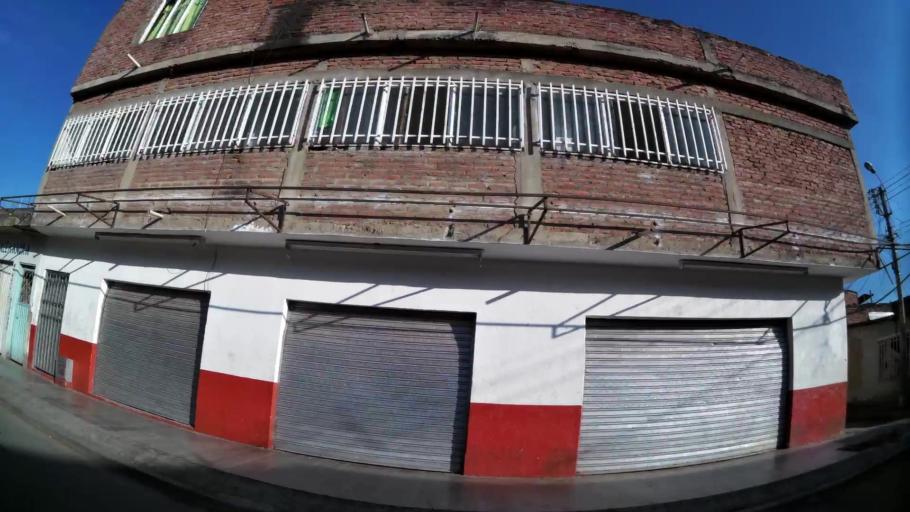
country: CO
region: Valle del Cauca
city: Cali
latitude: 3.4086
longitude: -76.4987
